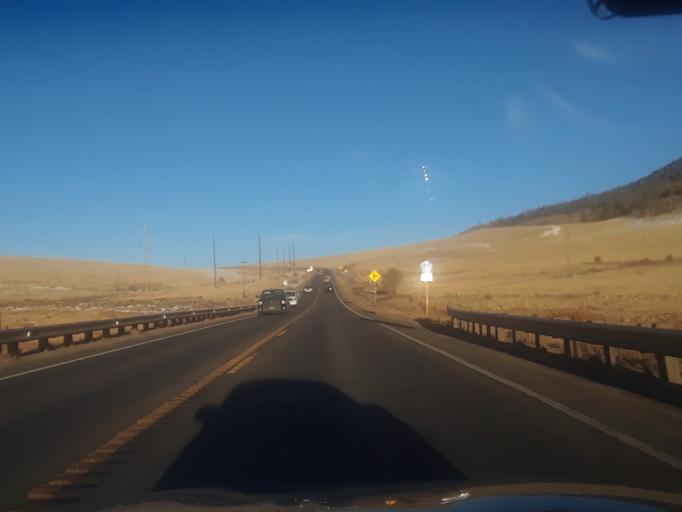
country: US
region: Colorado
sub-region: Park County
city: Fairplay
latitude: 39.2767
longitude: -105.9290
